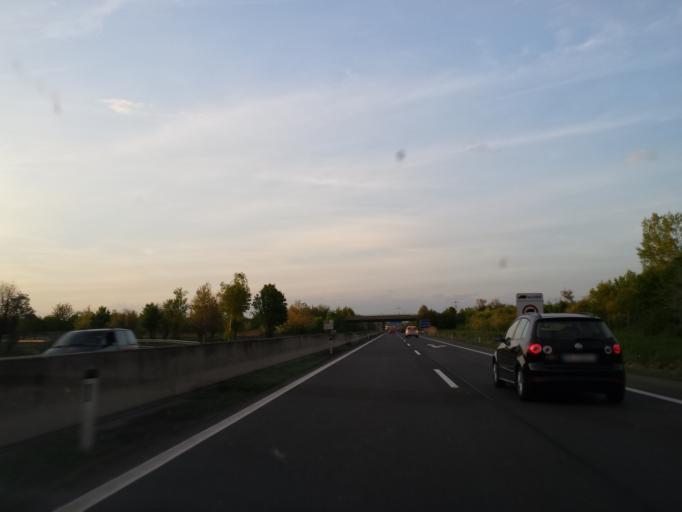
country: AT
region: Burgenland
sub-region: Politischer Bezirk Neusiedl am See
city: Parndorf
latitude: 48.0025
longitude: 16.8337
